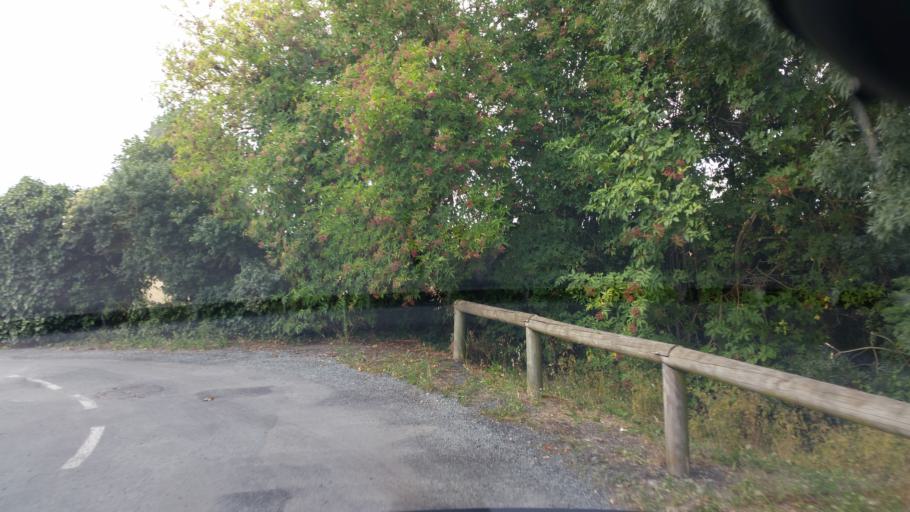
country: FR
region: Poitou-Charentes
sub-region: Departement de la Charente-Maritime
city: Marans
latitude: 46.3078
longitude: -0.9854
